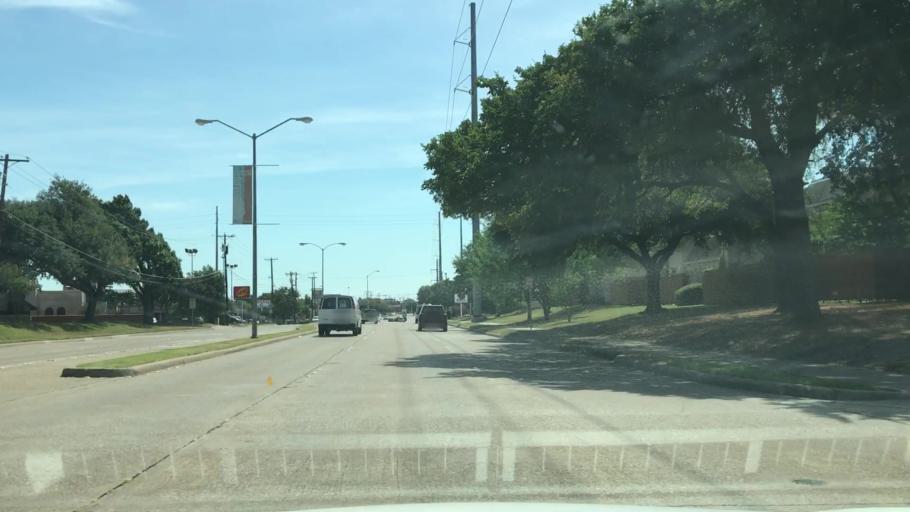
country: US
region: Texas
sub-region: Dallas County
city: Richardson
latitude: 32.9452
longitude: -96.6858
